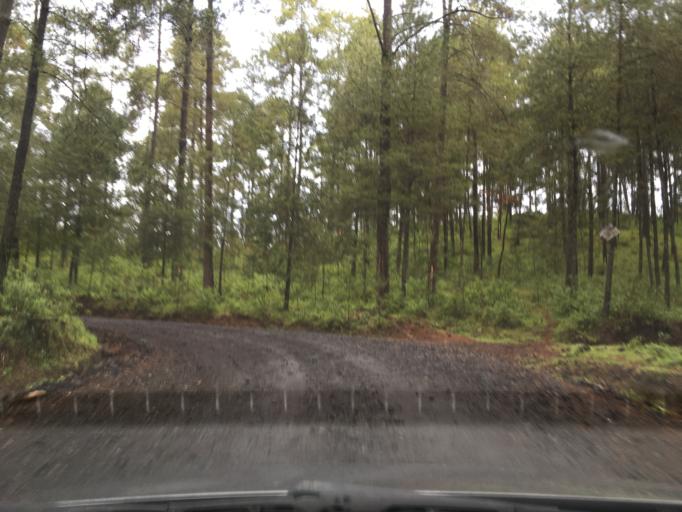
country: MX
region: Michoacan
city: Nuevo San Juan Parangaricutiro
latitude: 19.4619
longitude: -102.1971
